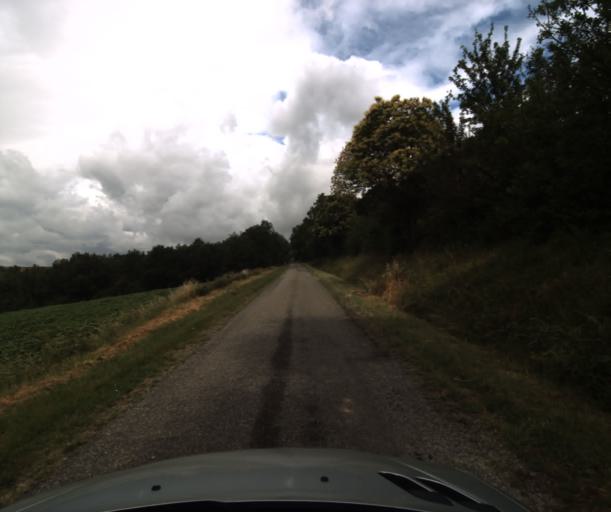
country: FR
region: Midi-Pyrenees
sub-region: Departement du Tarn-et-Garonne
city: Lavit
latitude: 43.9580
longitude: 0.8932
